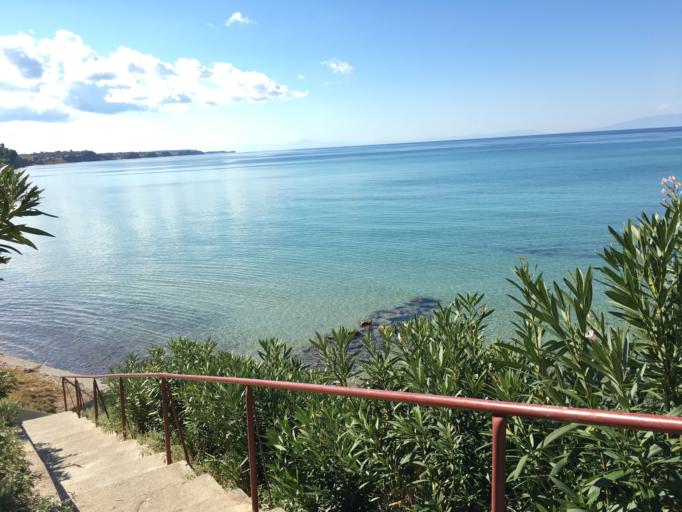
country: GR
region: Central Macedonia
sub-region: Nomos Chalkidikis
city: Nea Poteidaia
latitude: 40.1951
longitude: 23.3242
